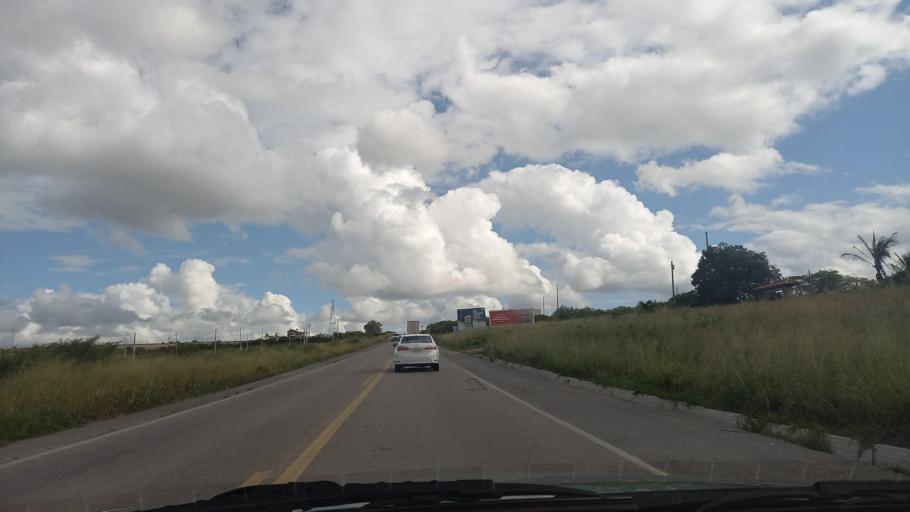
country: BR
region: Pernambuco
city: Garanhuns
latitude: -8.8279
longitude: -36.4516
